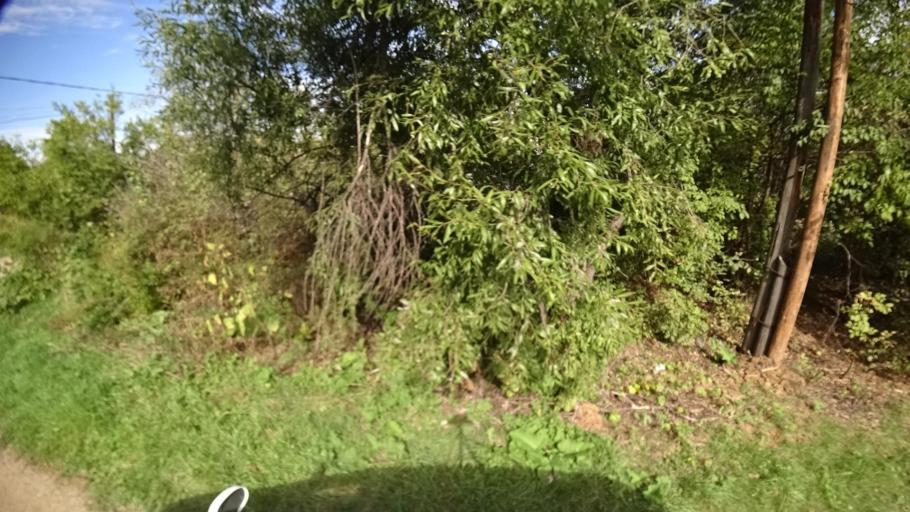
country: RU
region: Primorskiy
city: Yakovlevka
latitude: 44.3965
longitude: 133.6000
